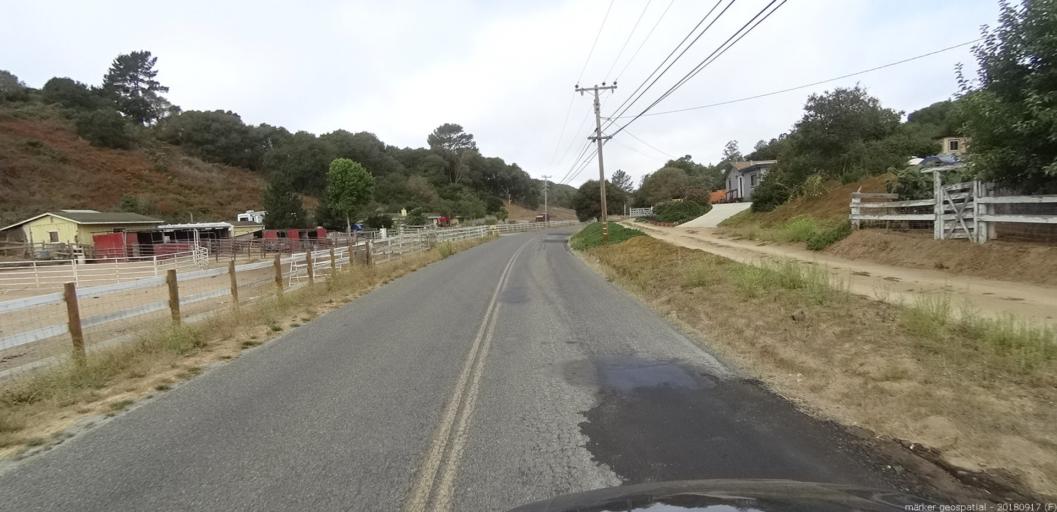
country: US
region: California
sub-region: Monterey County
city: Prunedale
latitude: 36.8021
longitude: -121.7020
